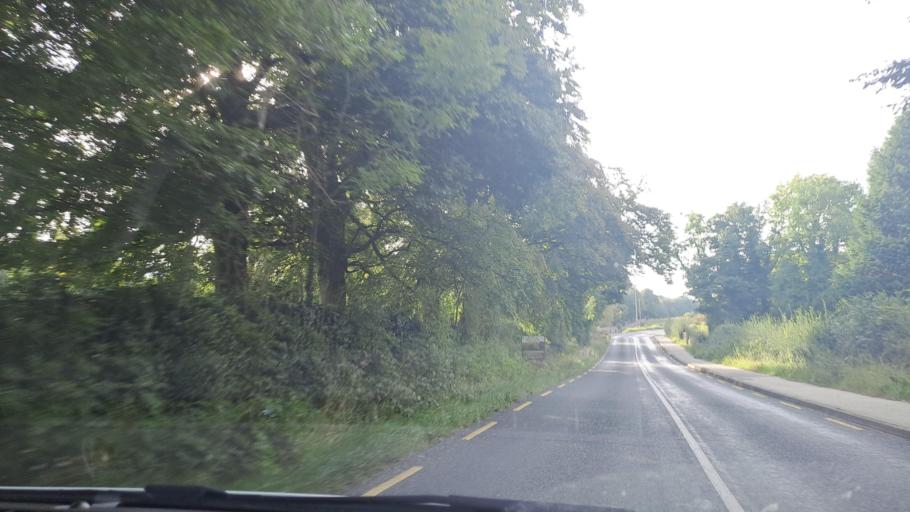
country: IE
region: Ulster
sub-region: An Cabhan
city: Kingscourt
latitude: 53.9148
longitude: -6.8066
